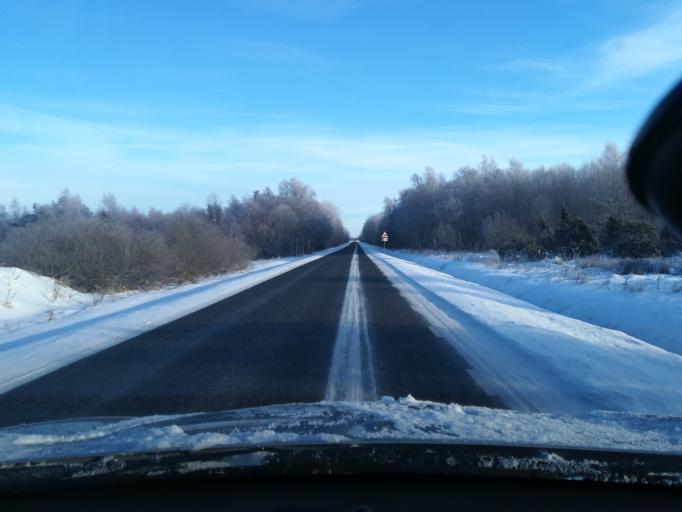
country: EE
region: Harju
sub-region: Keila linn
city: Keila
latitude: 59.3957
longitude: 24.3260
